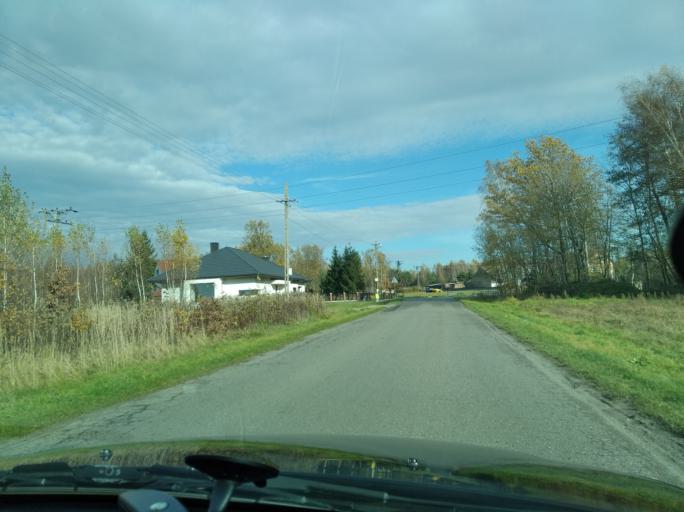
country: PL
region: Subcarpathian Voivodeship
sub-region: Powiat ropczycko-sedziszowski
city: Sedziszow Malopolski
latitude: 50.0998
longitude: 21.6607
